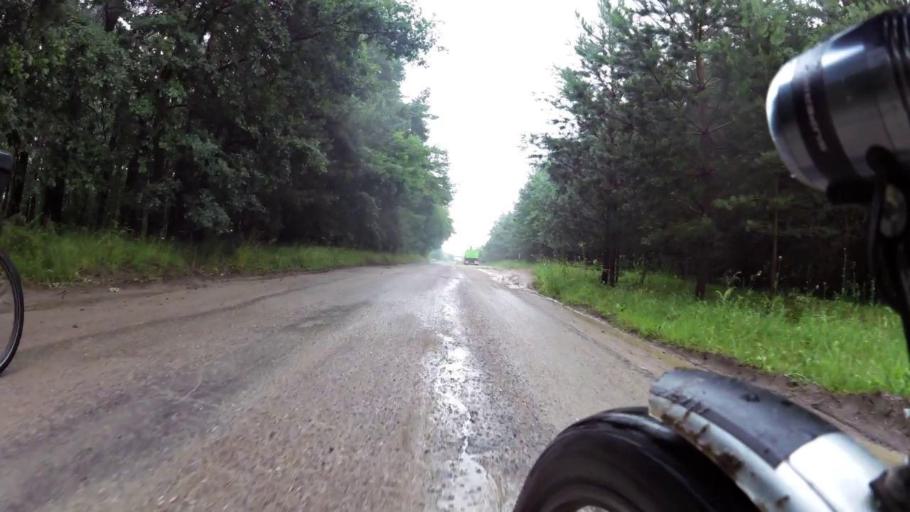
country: PL
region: West Pomeranian Voivodeship
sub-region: Powiat swidwinski
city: Swidwin
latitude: 53.7255
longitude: 15.6925
